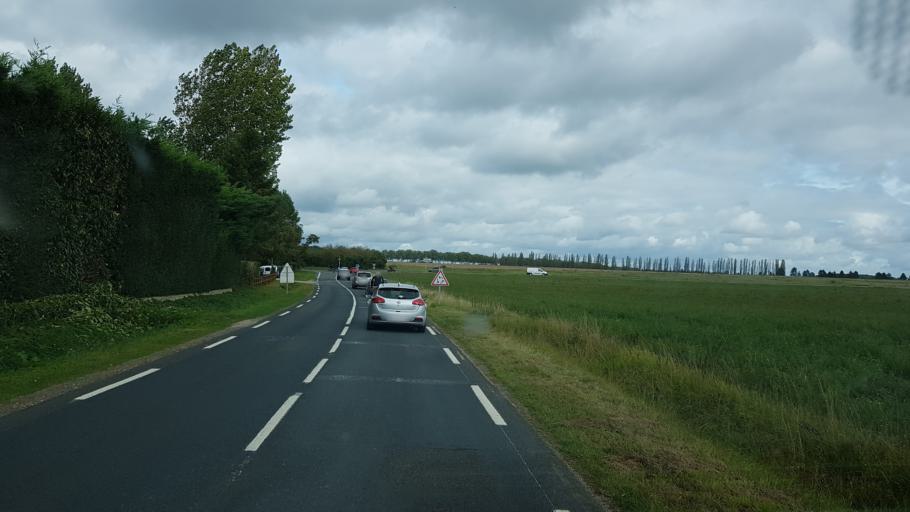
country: FR
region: Ile-de-France
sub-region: Departement des Yvelines
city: Cernay-la-Ville
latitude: 48.6671
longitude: 1.9885
